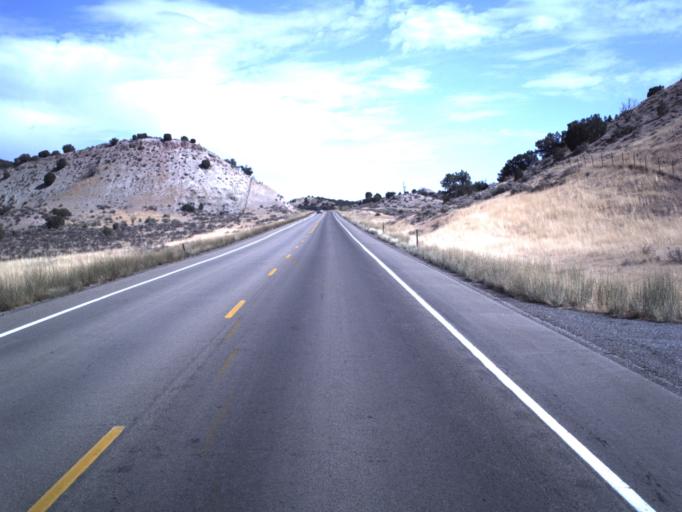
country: US
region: Utah
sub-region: Sanpete County
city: Gunnison
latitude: 39.3732
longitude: -111.9286
